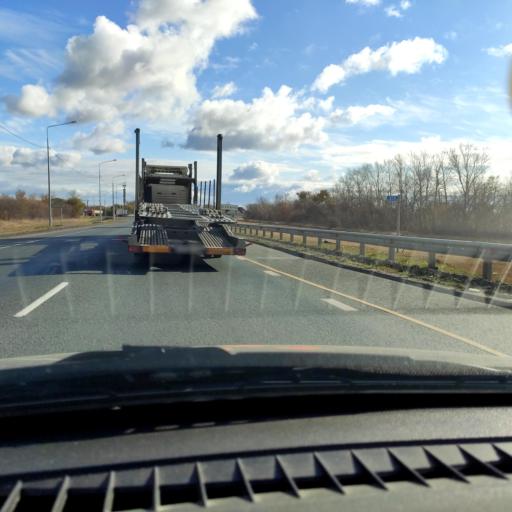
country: RU
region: Samara
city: Varlamovo
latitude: 53.1911
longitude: 48.3502
